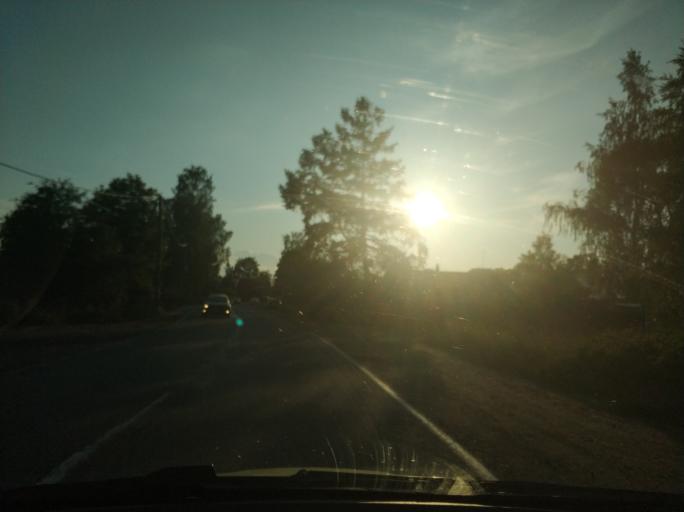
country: RU
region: Leningrad
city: Borisova Griva
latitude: 60.0936
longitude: 30.9800
